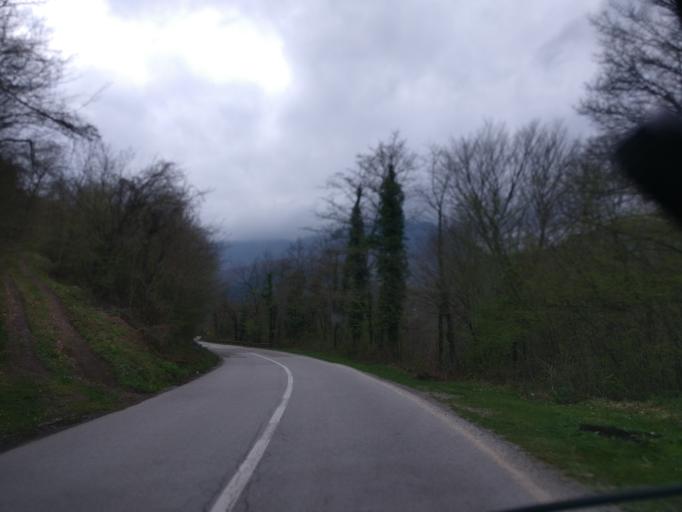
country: BA
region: Republika Srpska
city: Foca
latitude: 43.4682
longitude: 18.7474
